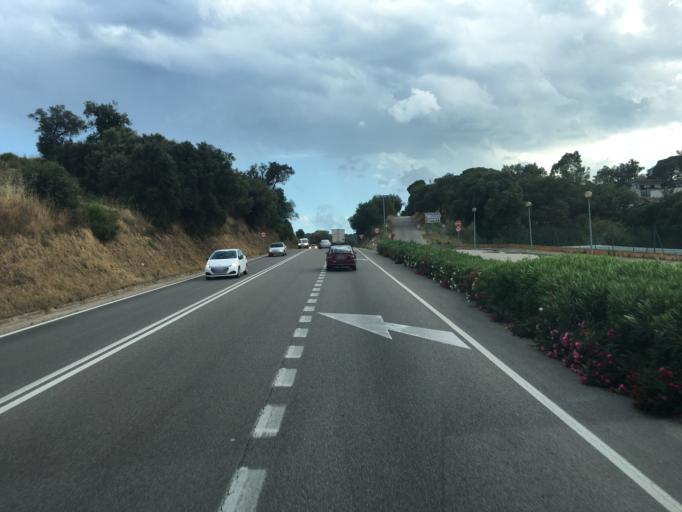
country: ES
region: Catalonia
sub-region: Provincia de Barcelona
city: Tordera
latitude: 41.6893
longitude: 2.7224
